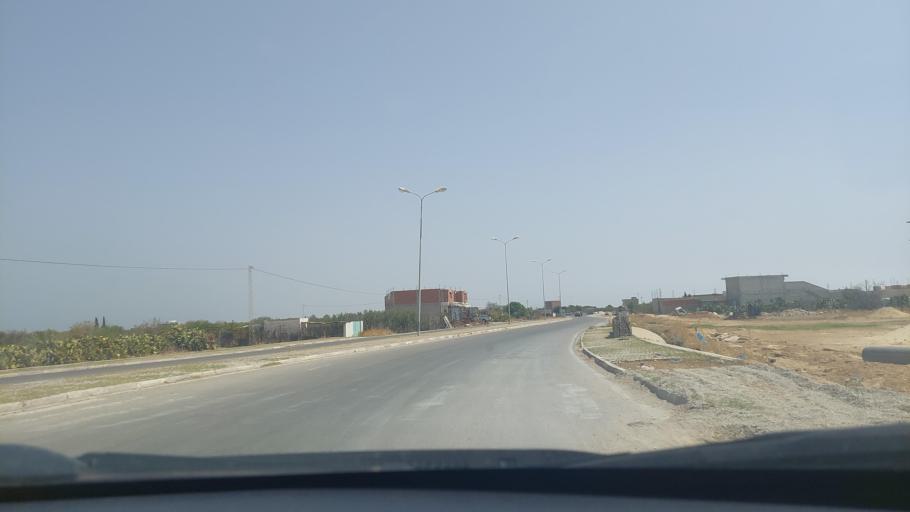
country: TN
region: Al Munastir
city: Qasr Hallal
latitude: 35.6038
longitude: 10.8907
